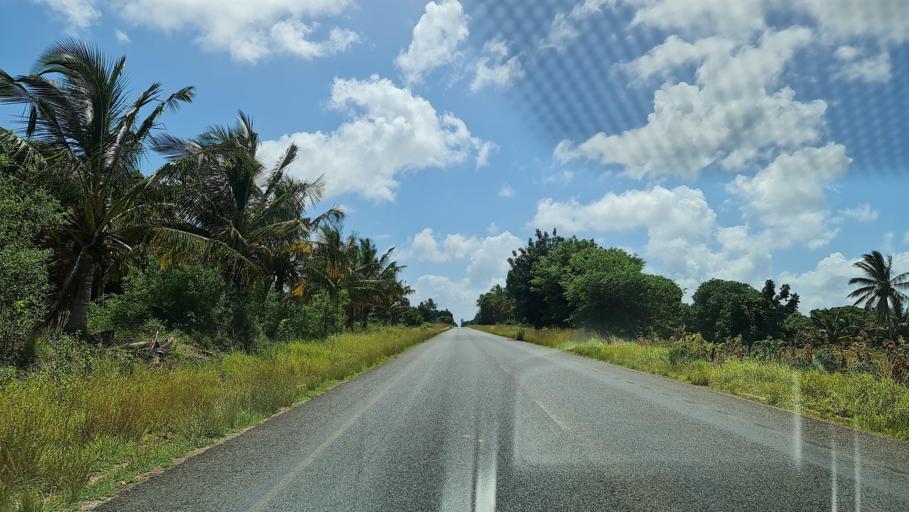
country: MZ
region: Inhambane
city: Maxixe
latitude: -24.5342
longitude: 34.9436
